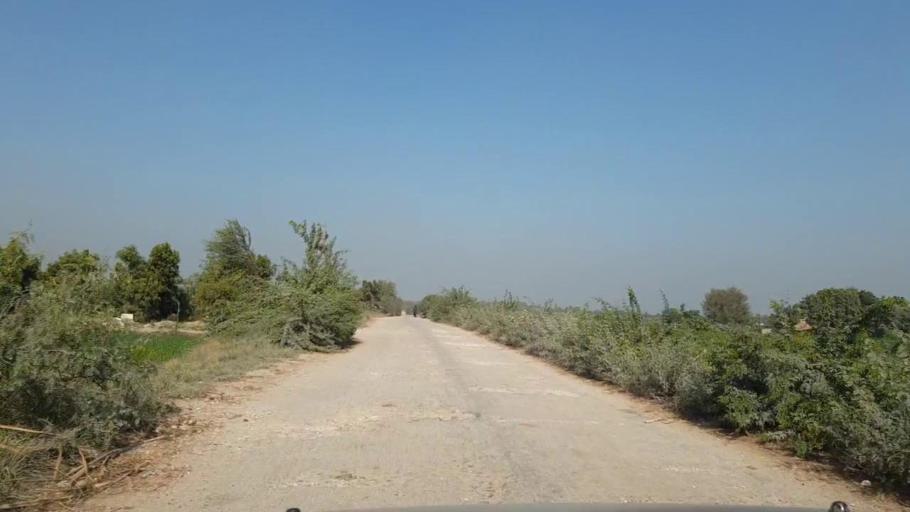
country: PK
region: Sindh
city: Matiari
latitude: 25.5800
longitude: 68.6037
